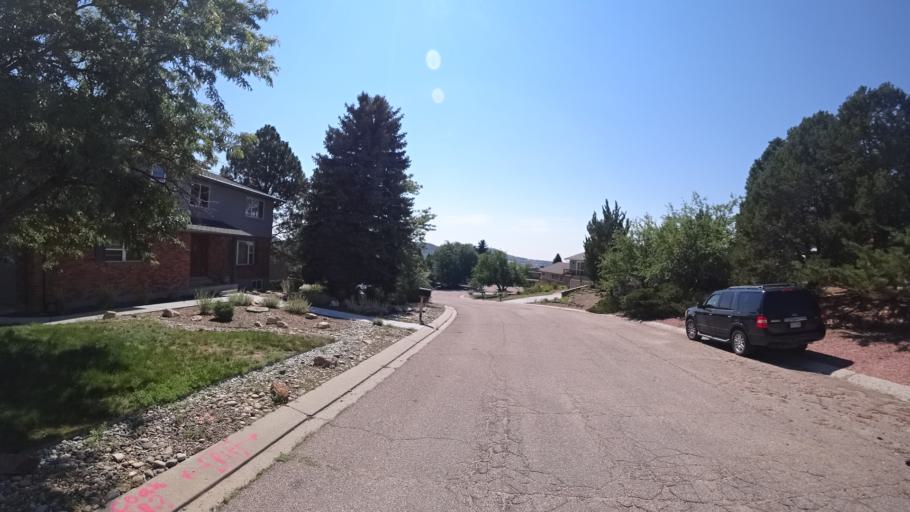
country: US
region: Colorado
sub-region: El Paso County
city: Air Force Academy
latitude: 38.9266
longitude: -104.8239
